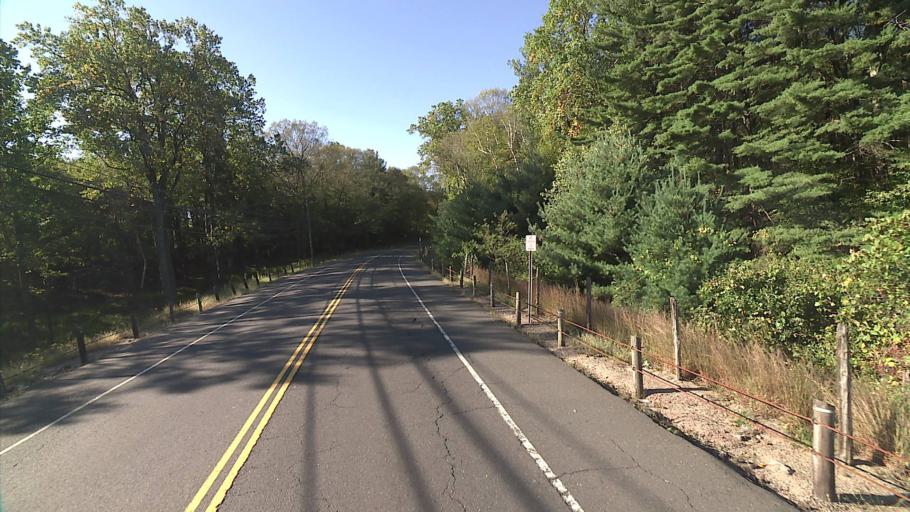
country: US
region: Connecticut
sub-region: New Haven County
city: Prospect
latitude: 41.5017
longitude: -72.9494
